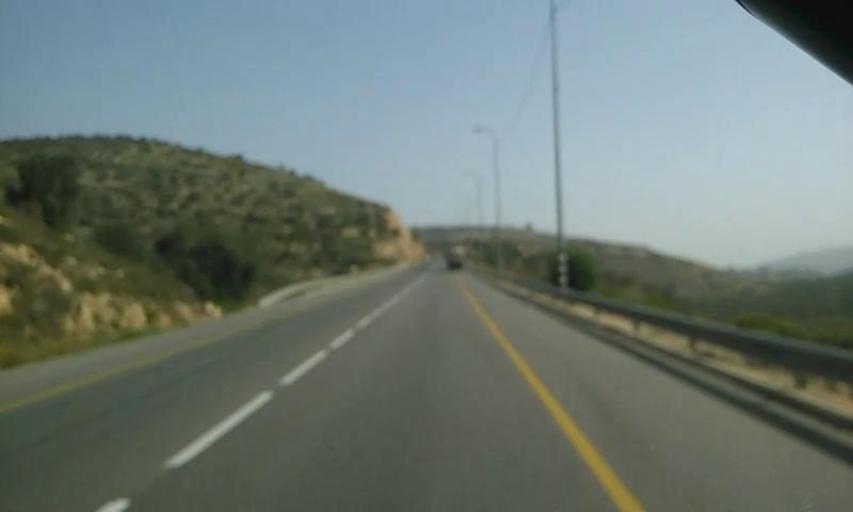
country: PS
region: West Bank
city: Yatma
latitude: 32.1079
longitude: 35.2564
